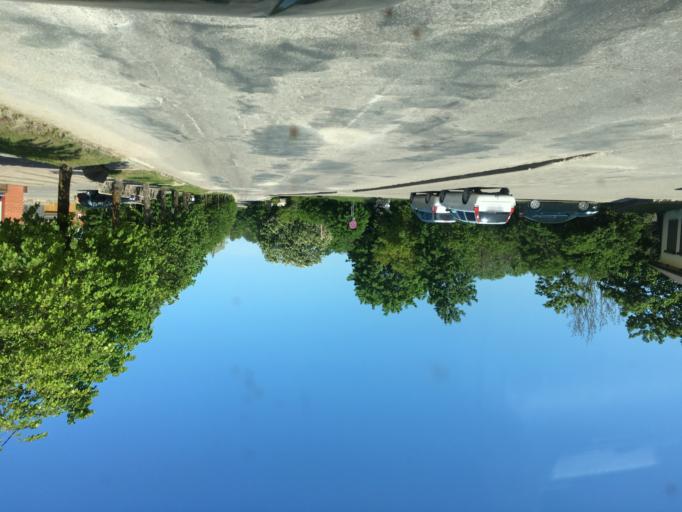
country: LV
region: Dundaga
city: Dundaga
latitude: 57.5098
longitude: 22.3509
